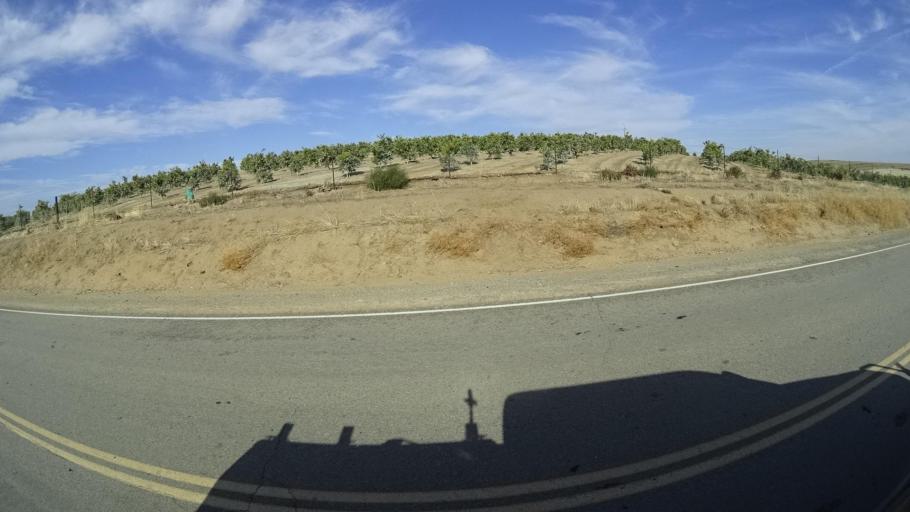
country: US
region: California
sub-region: Tulare County
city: Richgrove
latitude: 35.6185
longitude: -119.0463
